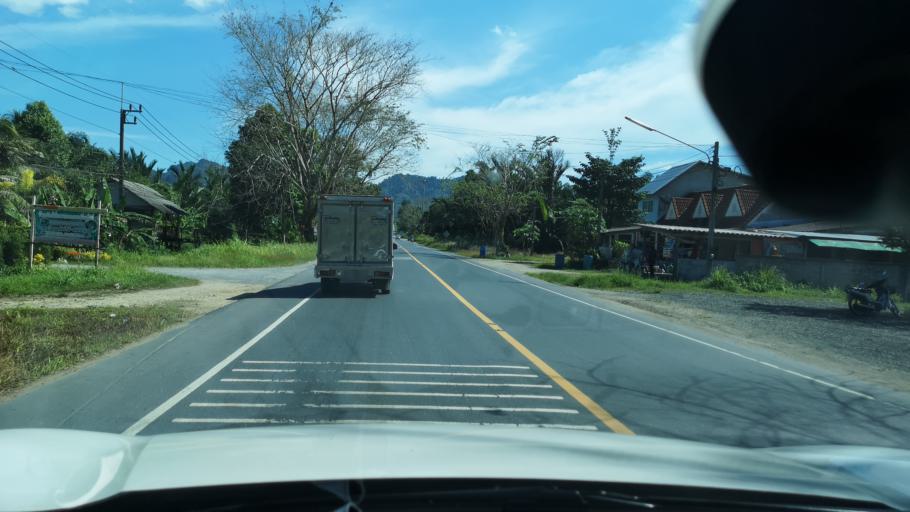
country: TH
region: Phangnga
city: Phang Nga
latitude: 8.5320
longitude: 98.5149
